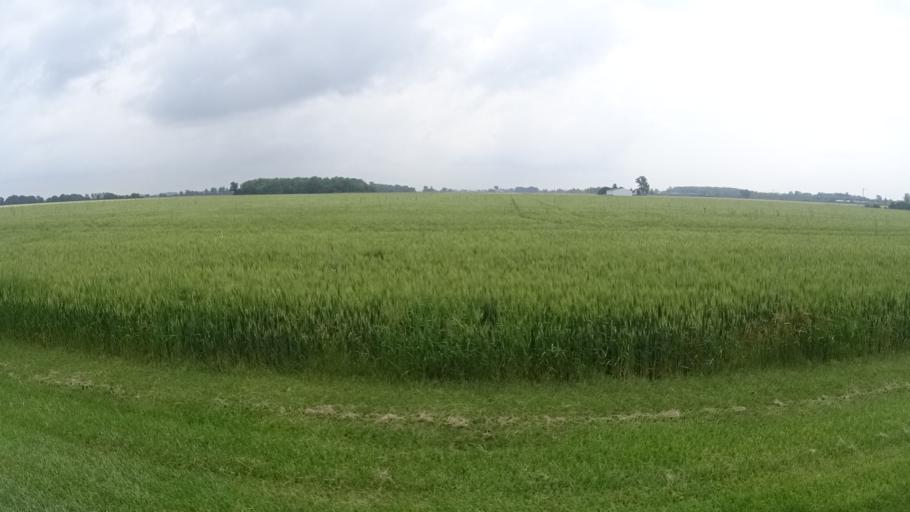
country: US
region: Ohio
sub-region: Huron County
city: Bellevue
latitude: 41.3000
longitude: -82.7923
